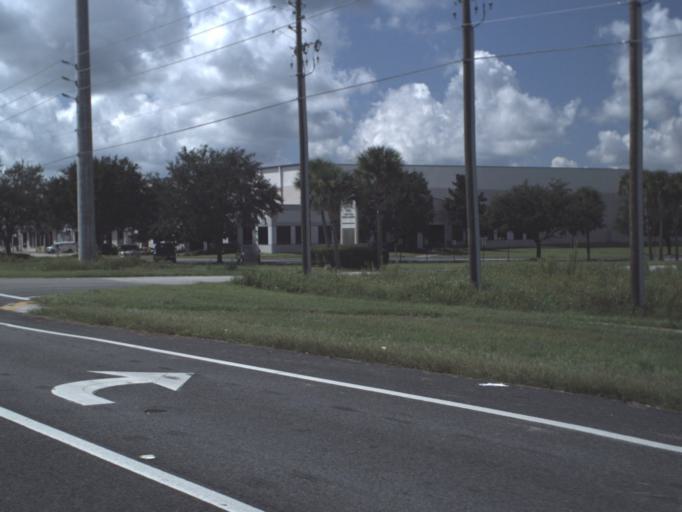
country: US
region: Florida
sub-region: Lake County
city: Four Corners
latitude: 28.2501
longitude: -81.6581
